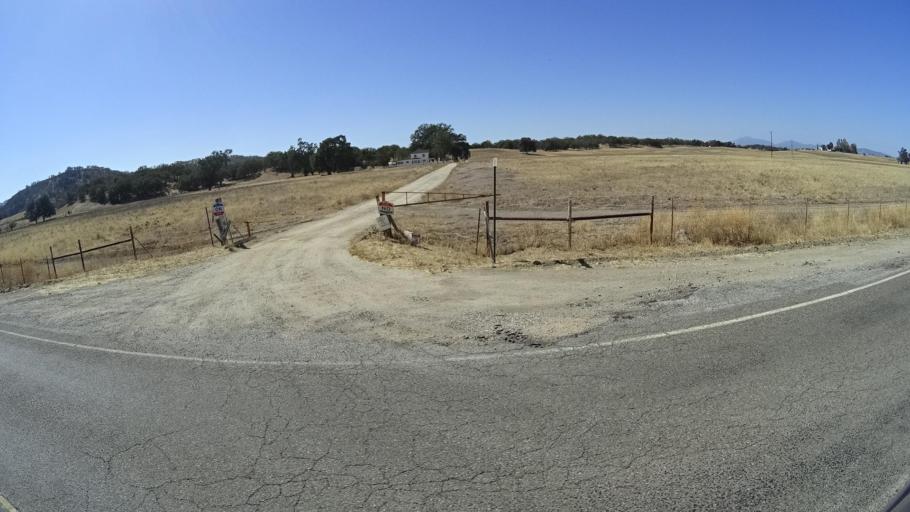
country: US
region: California
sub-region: San Luis Obispo County
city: Lake Nacimiento
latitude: 35.9256
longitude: -121.0817
